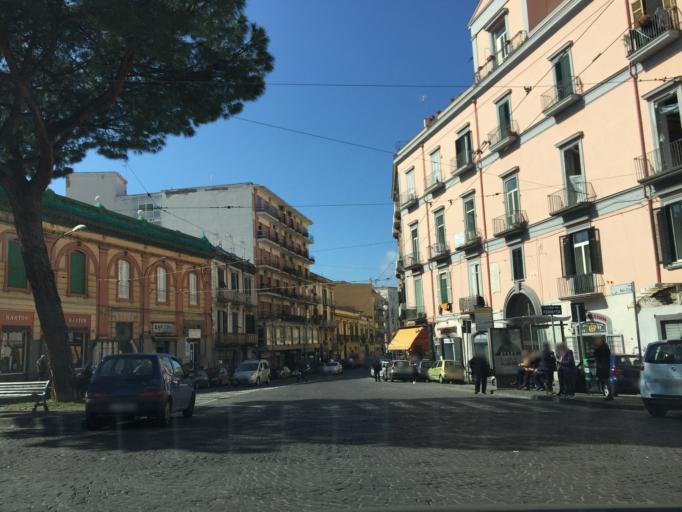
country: IT
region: Campania
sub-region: Provincia di Napoli
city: Portici
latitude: 40.8142
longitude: 14.3390
